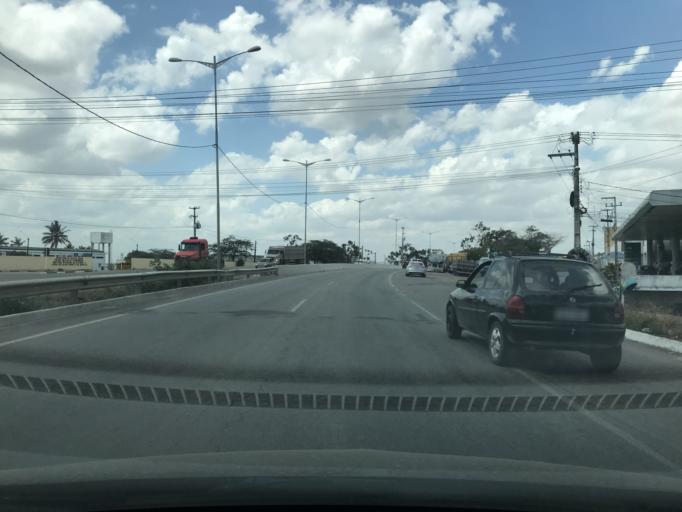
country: BR
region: Pernambuco
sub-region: Caruaru
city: Caruaru
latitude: -8.2970
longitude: -35.9882
